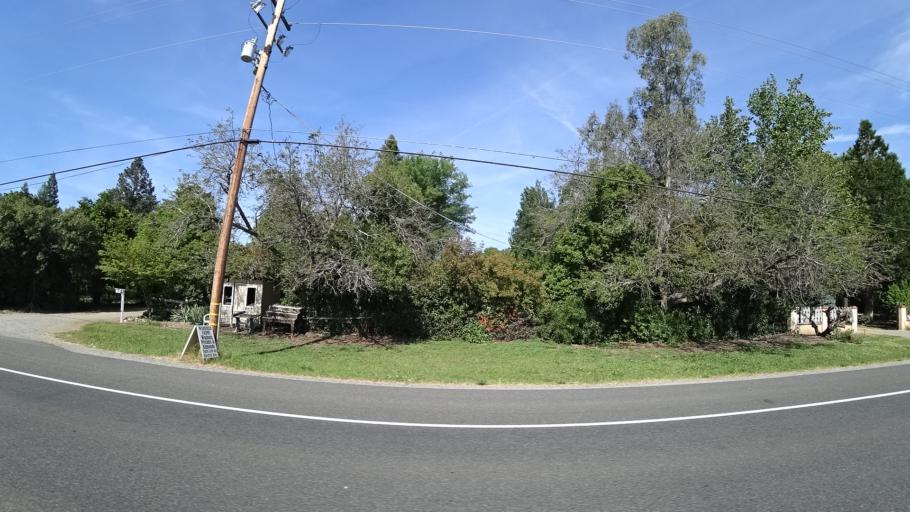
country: US
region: California
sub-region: Tehama County
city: Gerber
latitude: 40.1408
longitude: -122.1315
